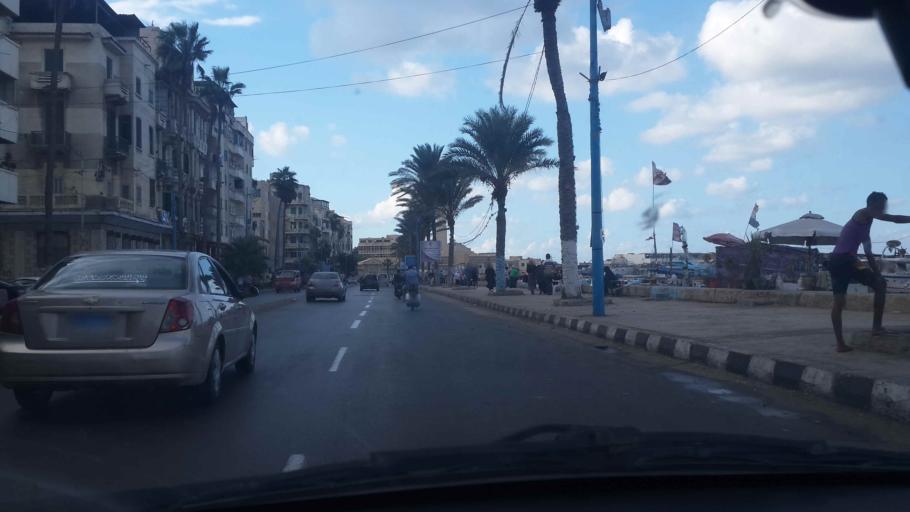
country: EG
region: Alexandria
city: Alexandria
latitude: 31.2076
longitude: 29.8833
